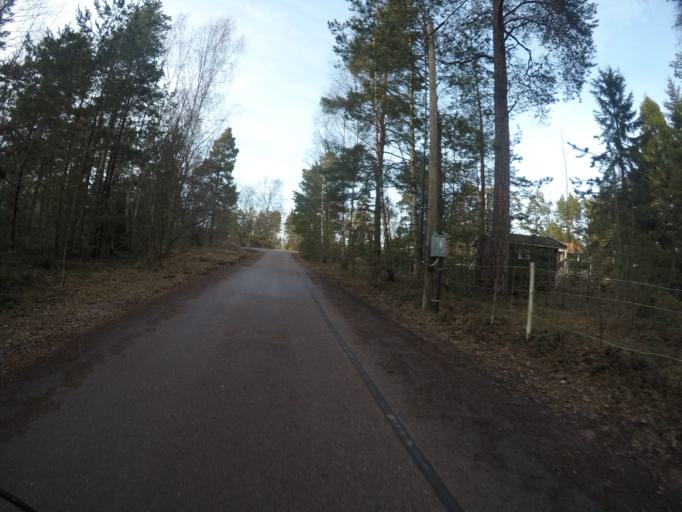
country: SE
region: Soedermanland
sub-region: Eskilstuna Kommun
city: Kvicksund
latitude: 59.4617
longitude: 16.3065
